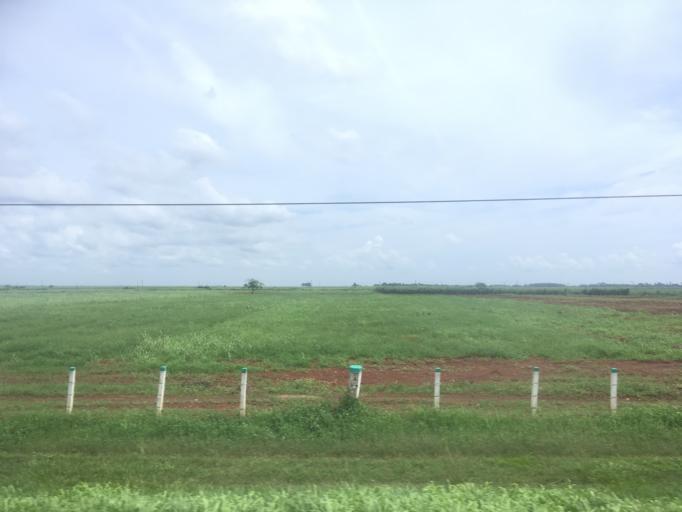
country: CU
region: Matanzas
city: Jovellanos
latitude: 22.7973
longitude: -81.1508
